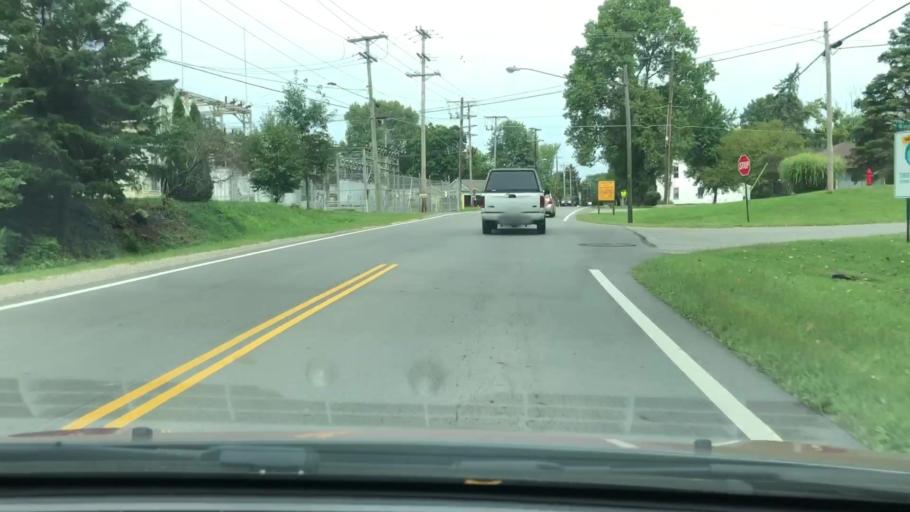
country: US
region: Ohio
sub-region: Delaware County
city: Sunbury
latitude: 40.2364
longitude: -82.8523
